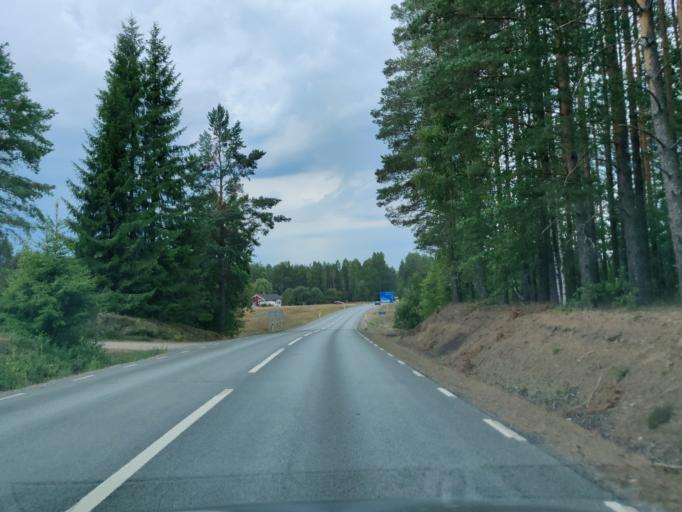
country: SE
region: Vaermland
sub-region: Hagfors Kommun
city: Hagfors
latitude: 59.9643
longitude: 13.5616
